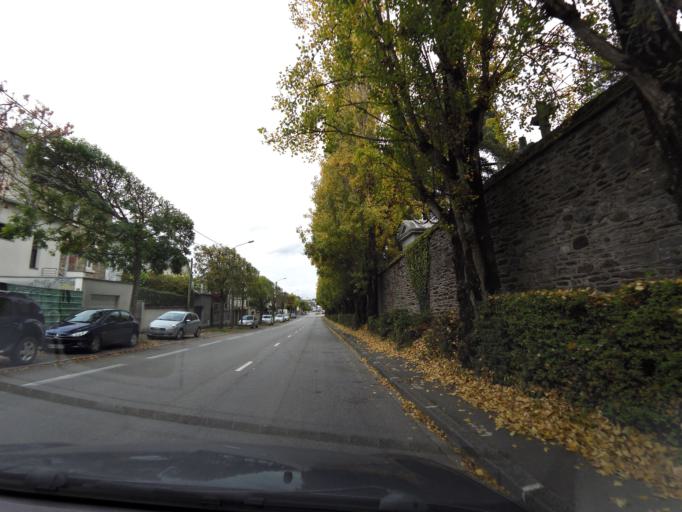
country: FR
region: Brittany
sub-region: Departement d'Ille-et-Vilaine
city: Rennes
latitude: 48.1260
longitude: -1.6825
